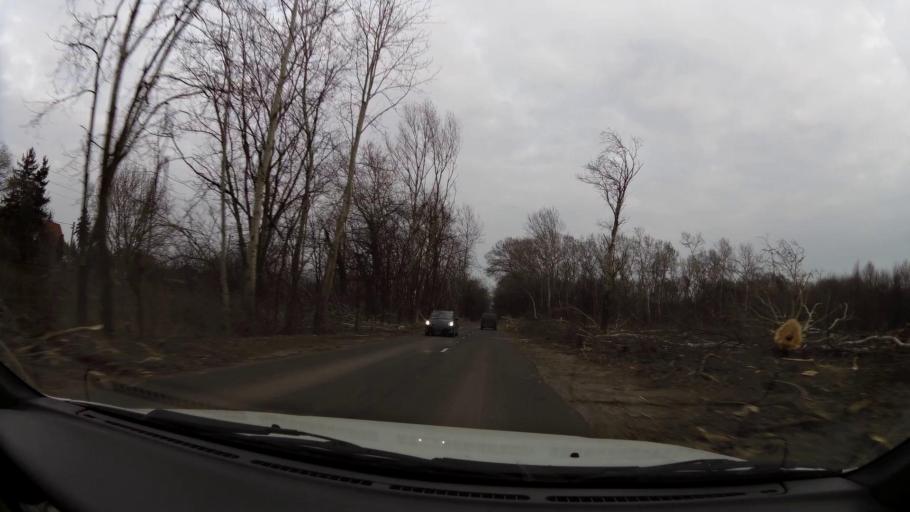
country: HU
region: Budapest
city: Budapest XVII. keruelet
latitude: 47.4785
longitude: 19.2135
